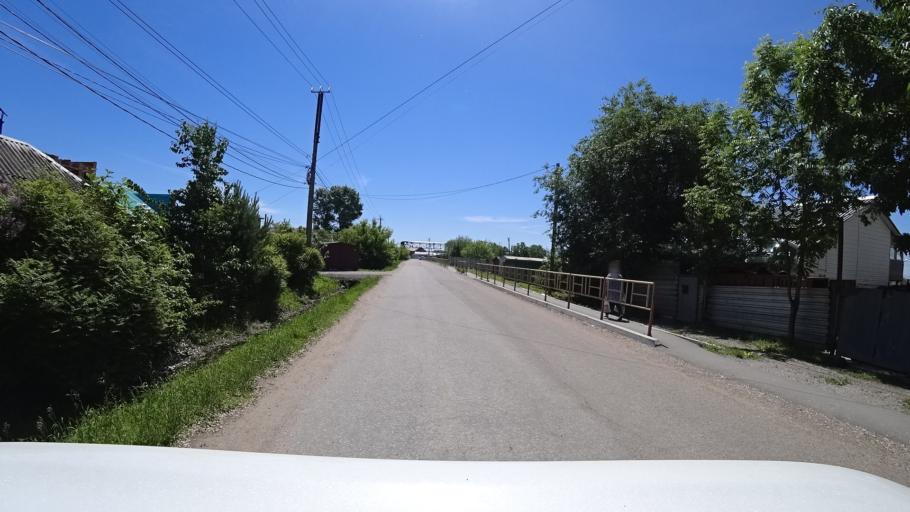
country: RU
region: Khabarovsk Krai
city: Topolevo
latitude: 48.5063
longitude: 135.1751
